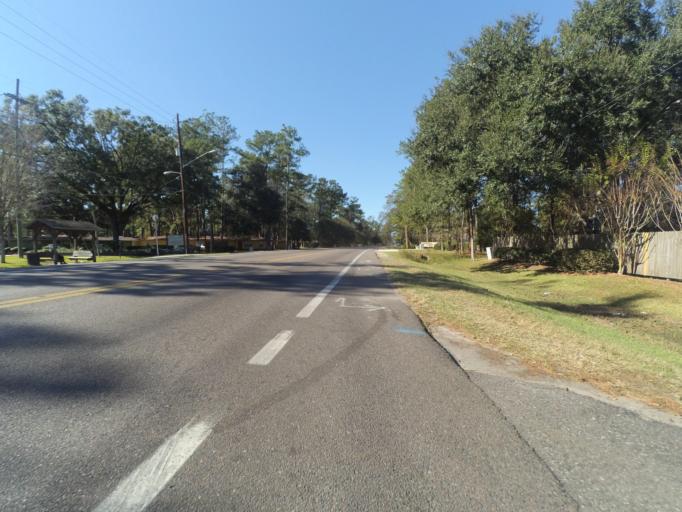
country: US
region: Florida
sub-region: Alachua County
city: Gainesville
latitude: 29.6343
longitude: -82.3846
